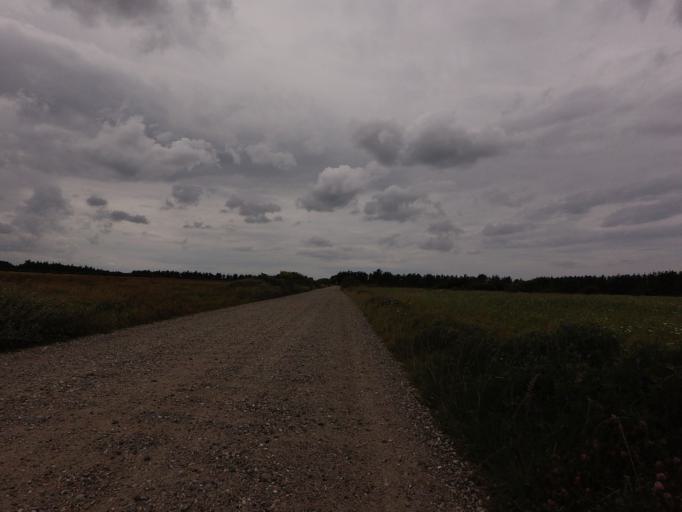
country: DK
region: North Denmark
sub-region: Jammerbugt Kommune
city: Pandrup
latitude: 57.3396
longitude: 9.6972
